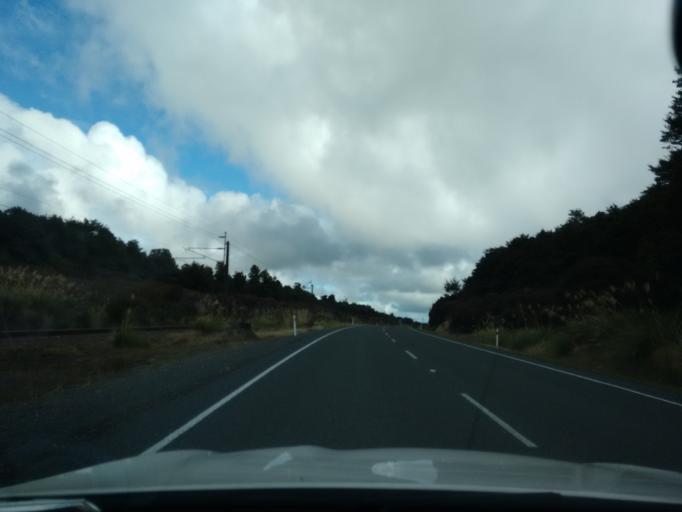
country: NZ
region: Manawatu-Wanganui
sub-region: Ruapehu District
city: Waiouru
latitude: -39.3071
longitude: 175.3898
